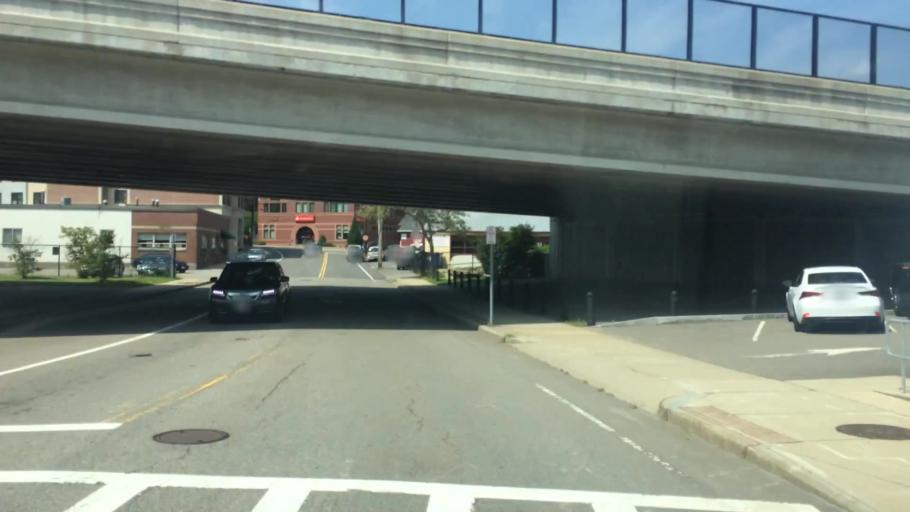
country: US
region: Massachusetts
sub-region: Norfolk County
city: Dedham
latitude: 42.2489
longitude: -71.1707
